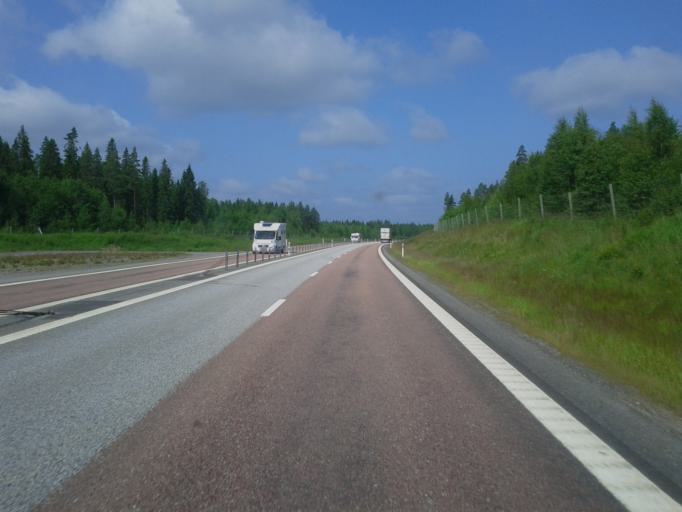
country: SE
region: Vaesterbotten
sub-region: Skelleftea Kommun
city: Soedra Bergsbyn
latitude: 64.6975
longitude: 21.0122
